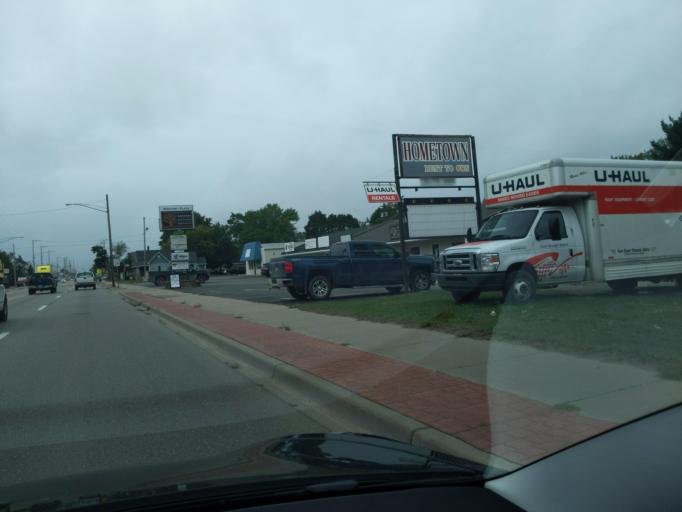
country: US
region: Michigan
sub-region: Wexford County
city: Cadillac
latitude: 44.2587
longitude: -85.4049
